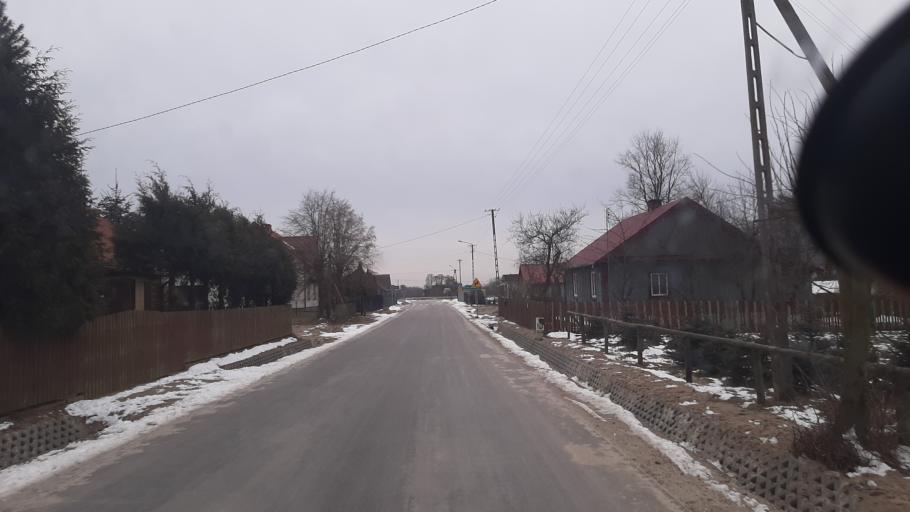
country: PL
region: Lublin Voivodeship
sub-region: Powiat lubartowski
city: Kamionka
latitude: 51.5141
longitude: 22.4721
